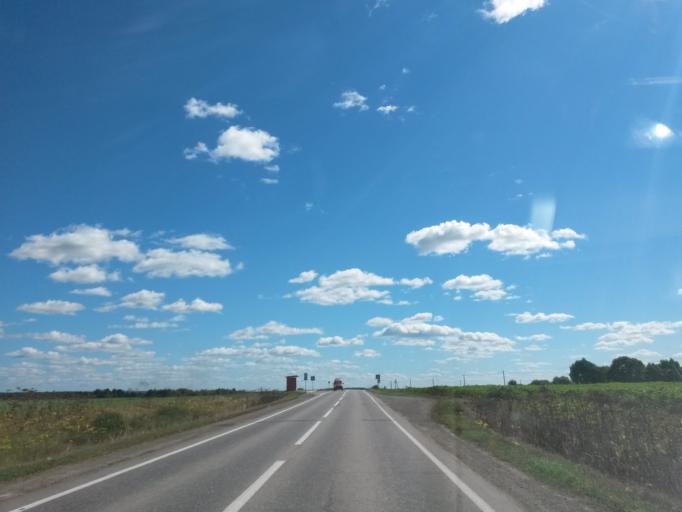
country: RU
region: Jaroslavl
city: Yaroslavl
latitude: 57.7598
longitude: 39.8668
